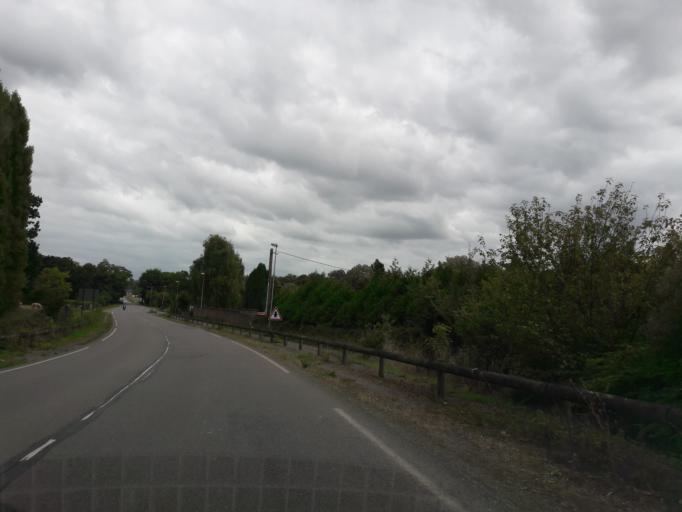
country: FR
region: Brittany
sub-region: Departement d'Ille-et-Vilaine
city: Bruz
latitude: 48.0206
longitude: -1.7259
